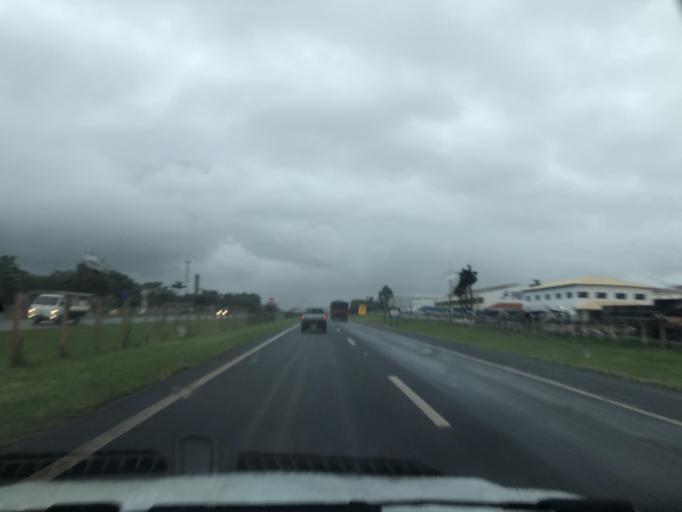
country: BR
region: Sao Paulo
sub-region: Ribeirao Preto
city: Ribeirao Preto
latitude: -21.0978
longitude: -47.7911
